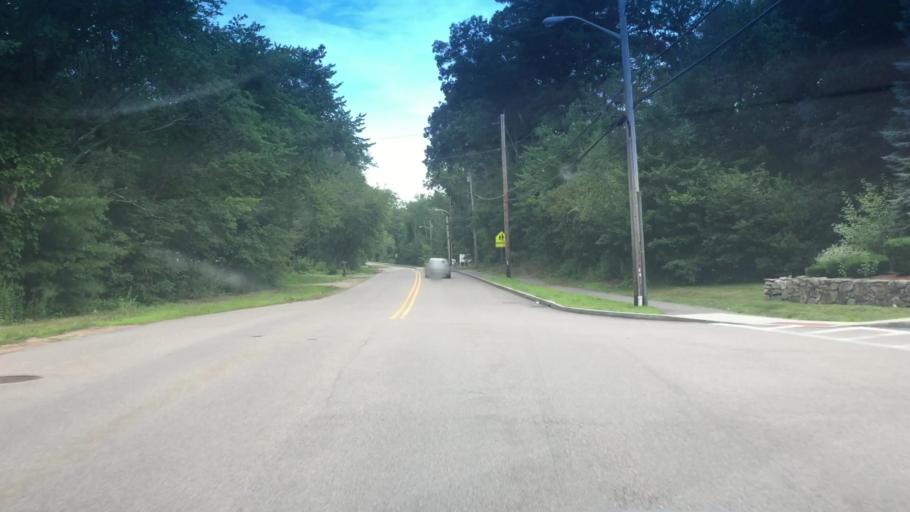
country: US
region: Massachusetts
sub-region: Norfolk County
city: Medway
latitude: 42.1150
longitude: -71.3959
